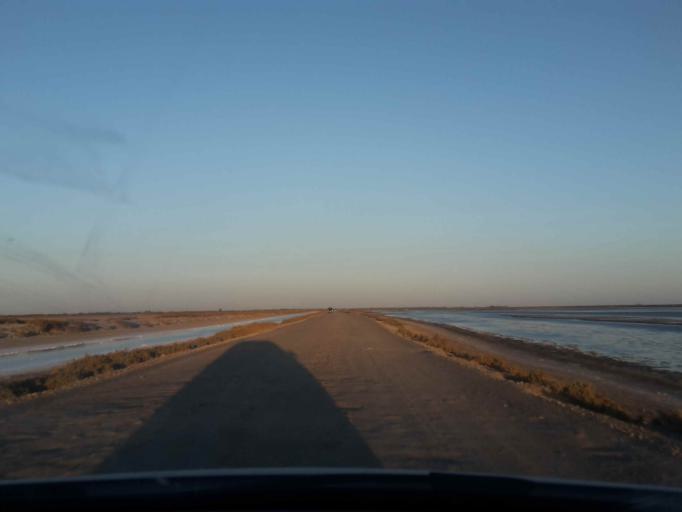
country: FR
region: Provence-Alpes-Cote d'Azur
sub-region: Departement des Bouches-du-Rhone
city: Port-Saint-Louis-du-Rhone
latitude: 43.4107
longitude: 4.6500
